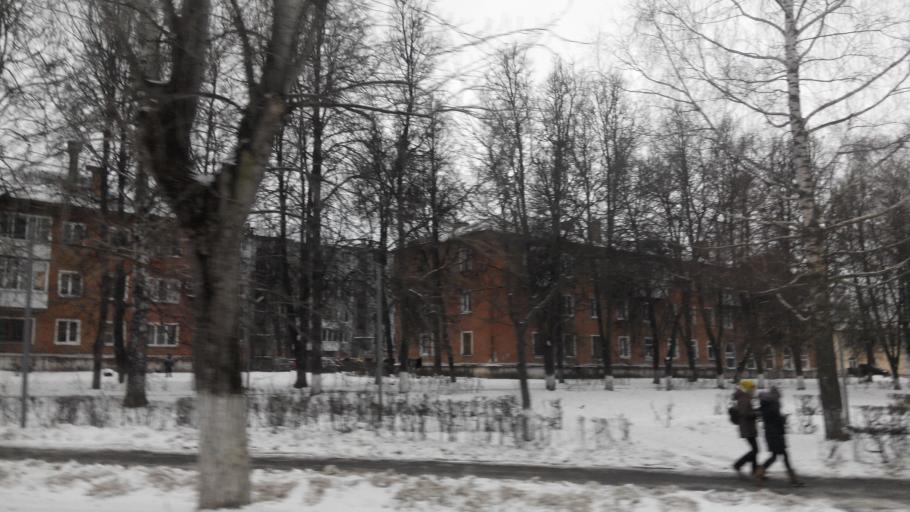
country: RU
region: Tula
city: Uzlovaya
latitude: 53.9692
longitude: 38.1677
